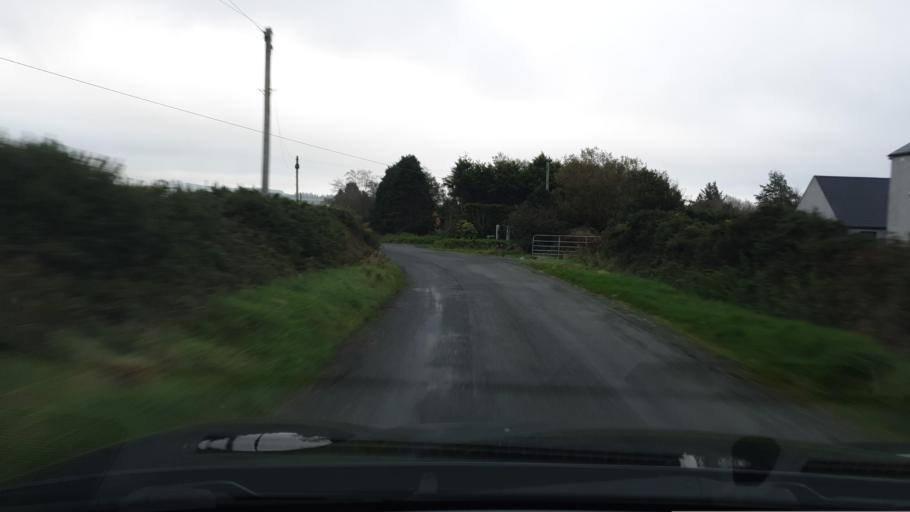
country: IE
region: Leinster
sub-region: Wicklow
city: Kilmacanoge
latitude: 53.1196
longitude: -6.1905
